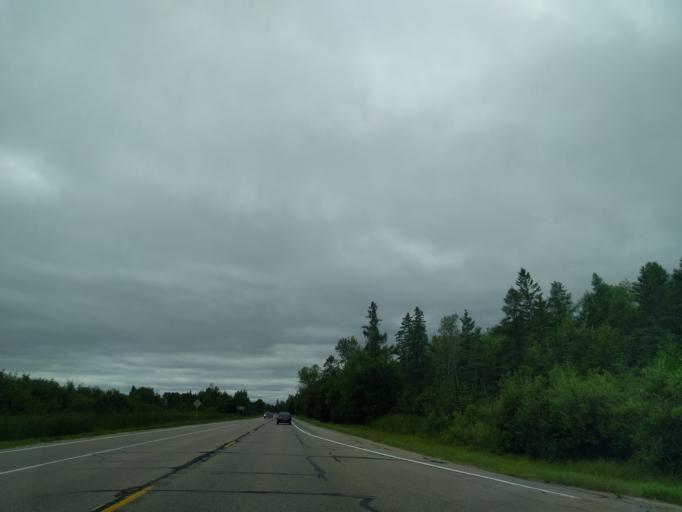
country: US
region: Michigan
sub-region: Delta County
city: Escanaba
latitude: 45.6760
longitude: -87.1455
